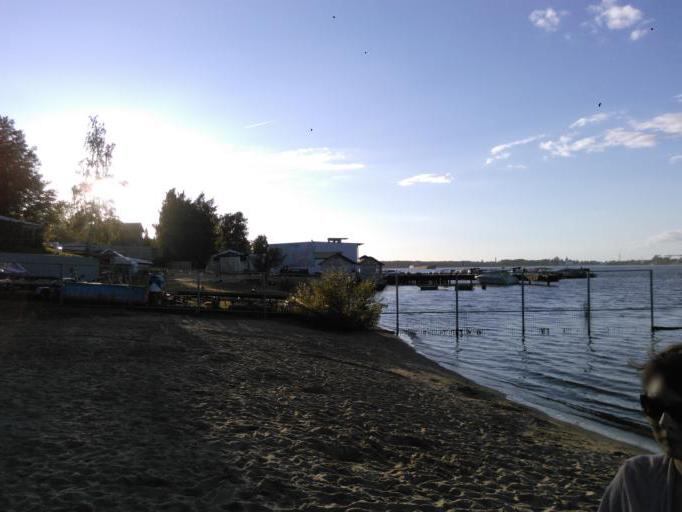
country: RU
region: Kostroma
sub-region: Kostromskoy Rayon
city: Kostroma
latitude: 57.7565
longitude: 40.9170
